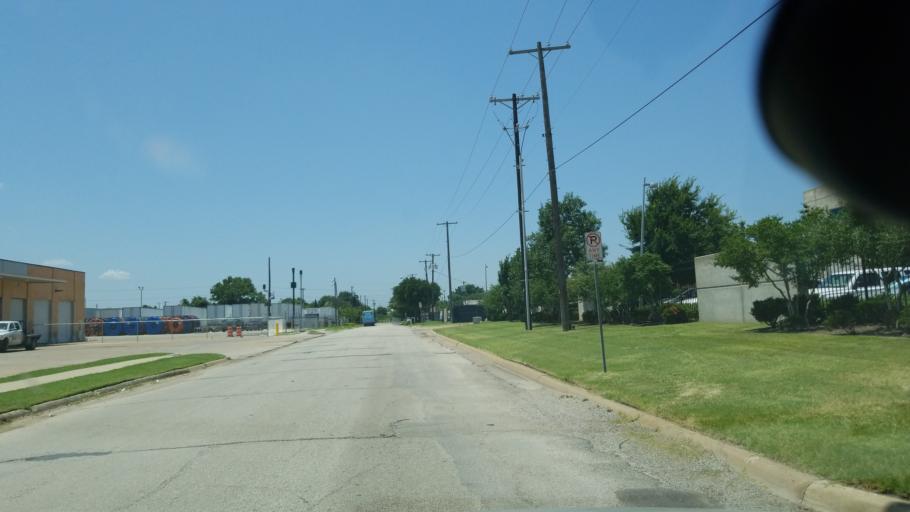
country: US
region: Texas
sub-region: Dallas County
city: Irving
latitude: 32.8174
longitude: -96.8775
